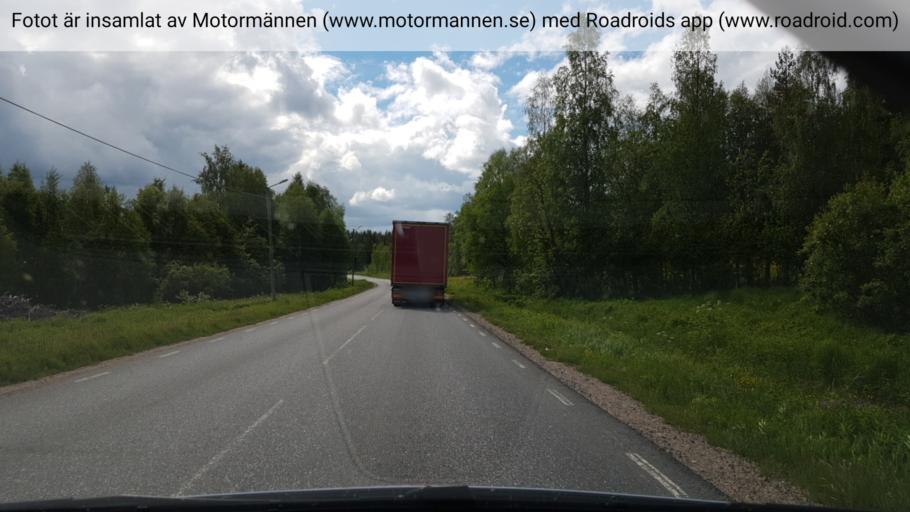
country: FI
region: Lapland
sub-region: Torniolaakso
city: Ylitornio
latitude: 66.2647
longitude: 23.6511
